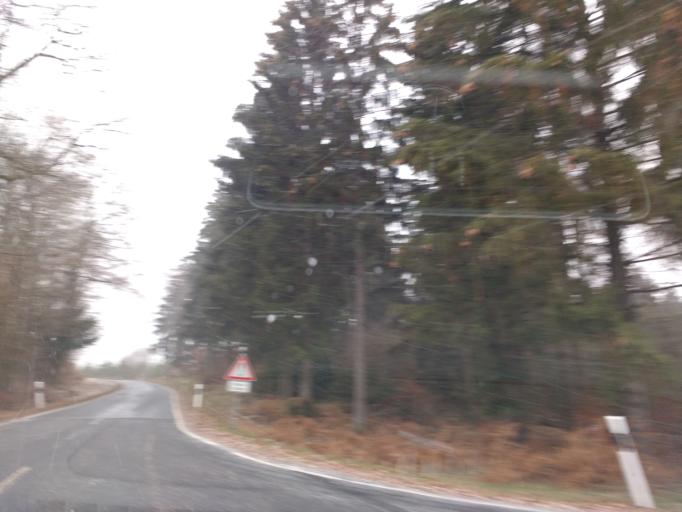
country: DE
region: Hesse
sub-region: Regierungsbezirk Kassel
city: Cornberg
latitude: 51.0833
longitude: 9.7912
